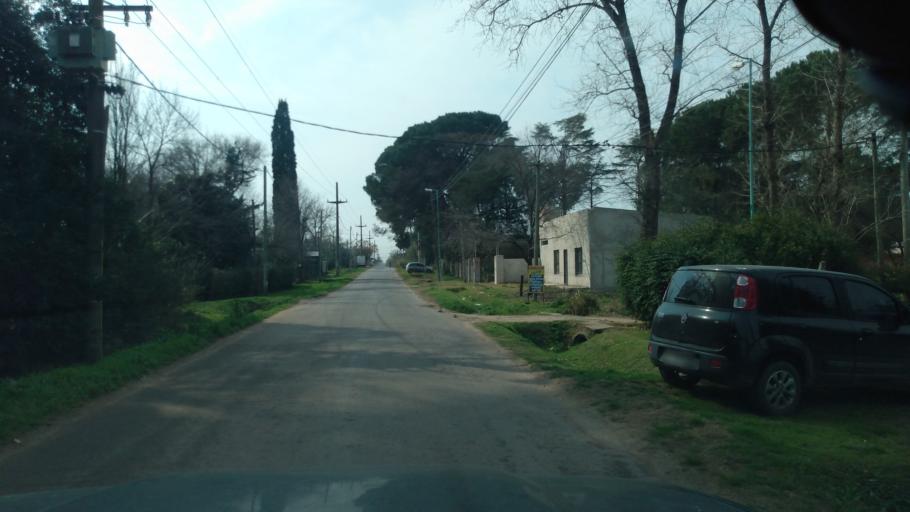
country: AR
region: Buenos Aires
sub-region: Partido de Lujan
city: Lujan
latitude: -34.4924
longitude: -59.0814
